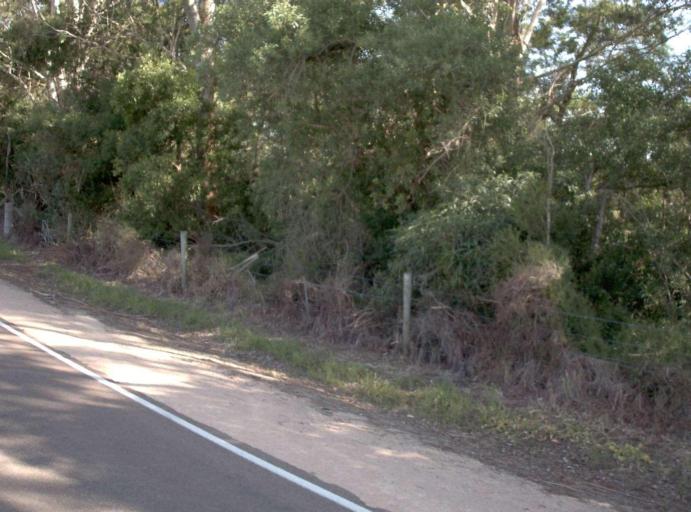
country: AU
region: Victoria
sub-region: East Gippsland
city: Lakes Entrance
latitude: -37.7245
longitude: 148.4987
